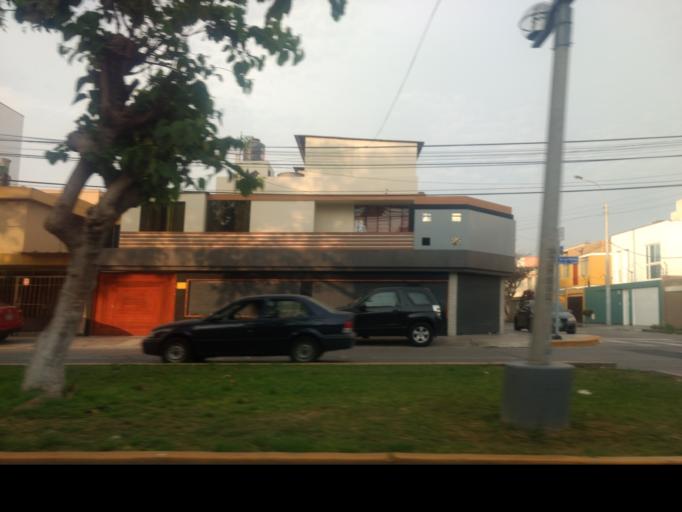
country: PE
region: Callao
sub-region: Callao
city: Callao
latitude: -12.0755
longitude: -77.1013
